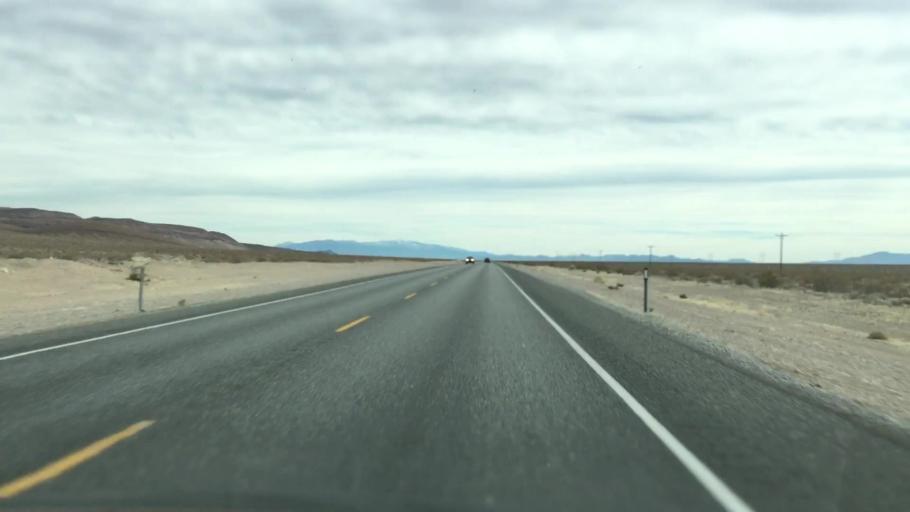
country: US
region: Nevada
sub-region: Nye County
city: Beatty
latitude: 36.7012
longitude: -116.5832
